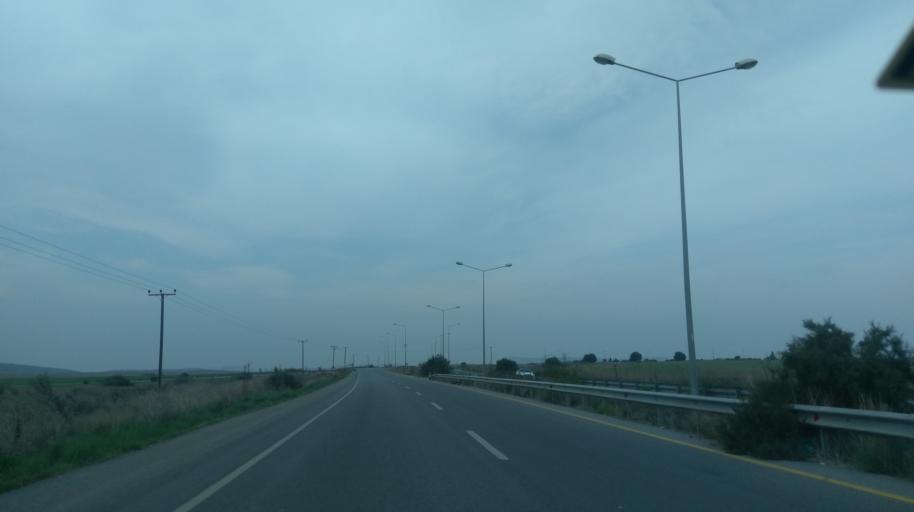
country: CY
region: Lefkosia
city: Mammari
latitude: 35.2109
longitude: 33.2240
